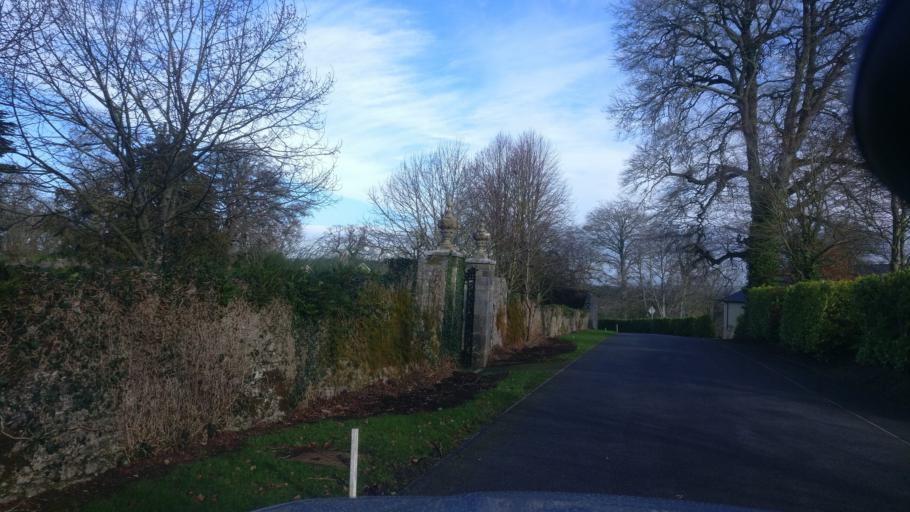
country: IE
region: Leinster
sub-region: Kilkenny
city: Thomastown
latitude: 52.5266
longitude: -7.1903
